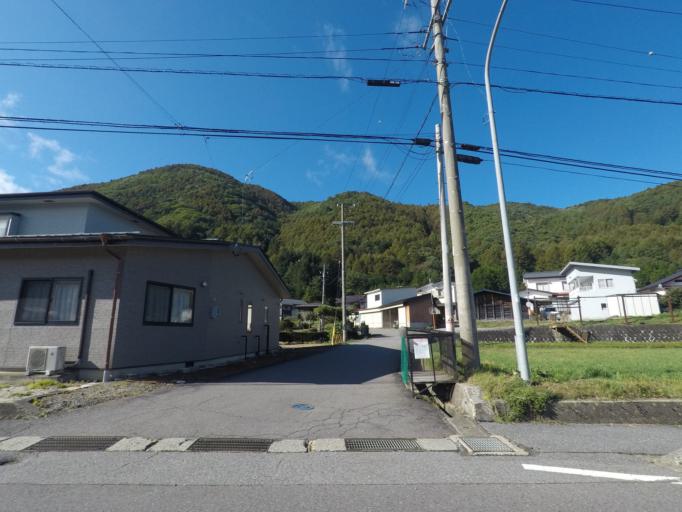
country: JP
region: Nagano
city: Ina
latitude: 35.9494
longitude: 137.7758
